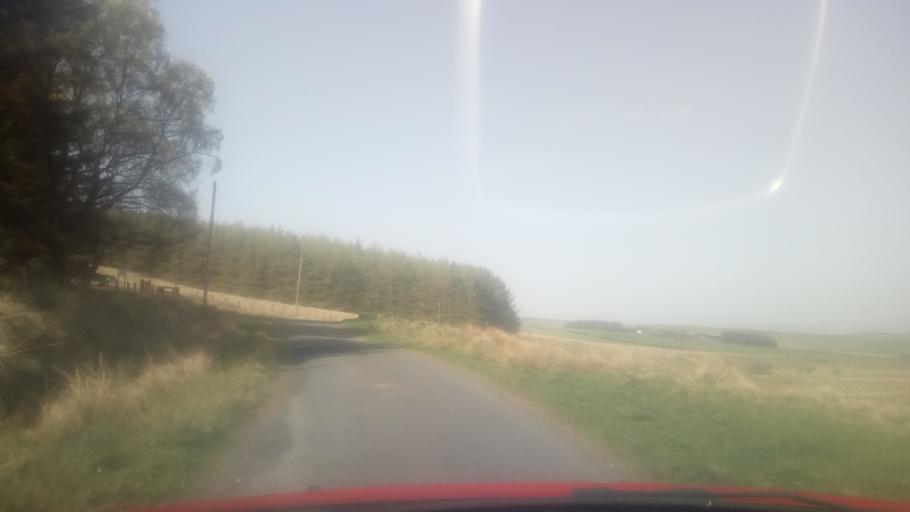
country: GB
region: England
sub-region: Northumberland
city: Rochester
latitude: 55.4138
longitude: -2.3826
